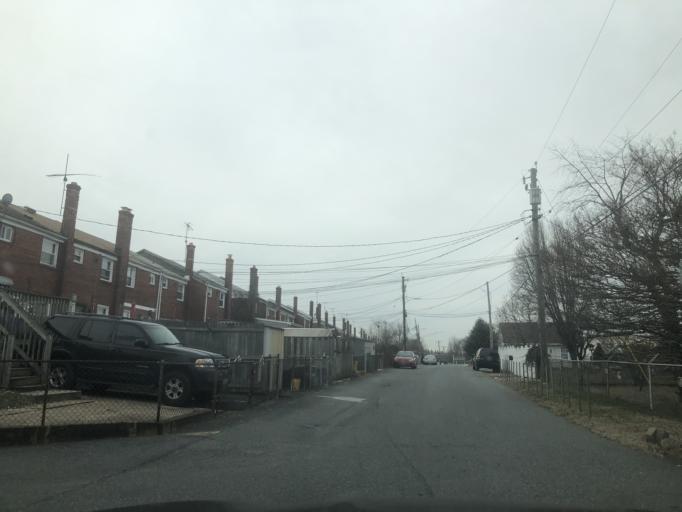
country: US
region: Maryland
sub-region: Baltimore County
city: Edgemere
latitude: 39.2568
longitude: -76.4820
